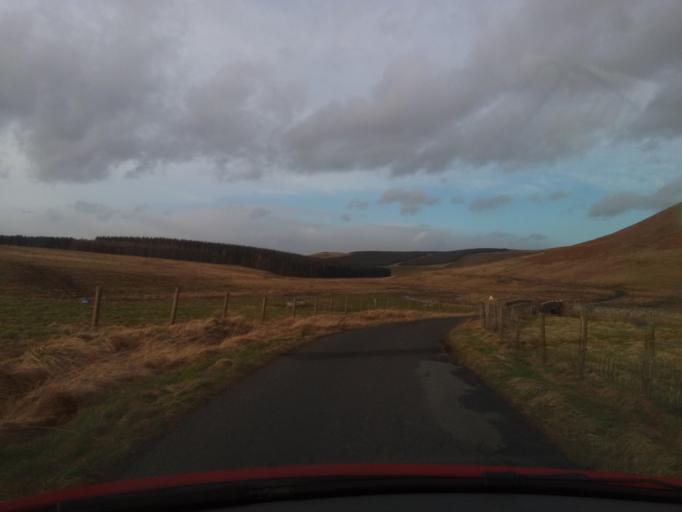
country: GB
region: Scotland
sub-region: The Scottish Borders
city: Jedburgh
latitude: 55.4190
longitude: -2.4155
